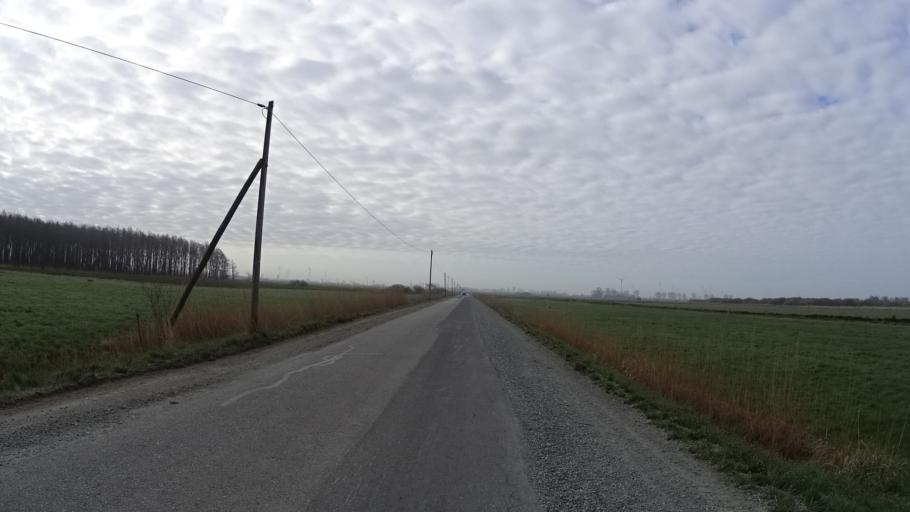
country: DE
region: Lower Saxony
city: Emden
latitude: 53.4103
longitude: 7.3053
